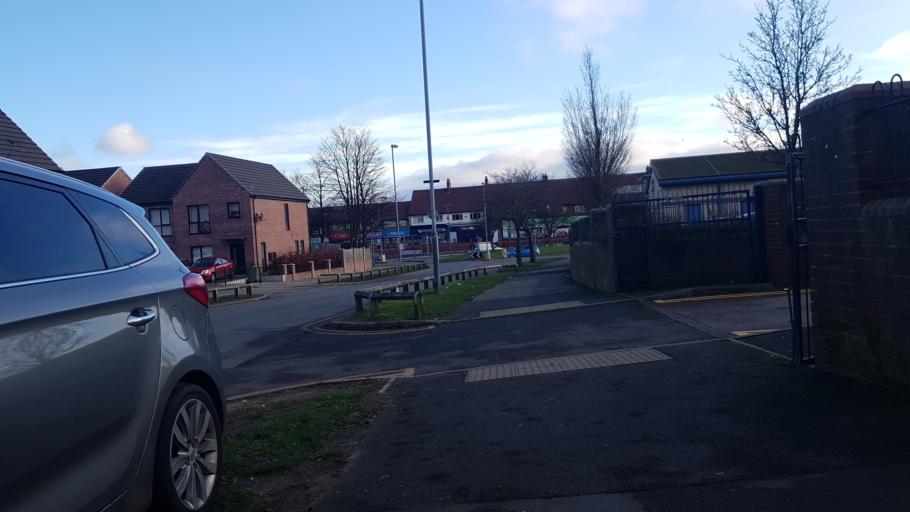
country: GB
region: England
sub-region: City and Borough of Wakefield
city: Pontefract
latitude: 53.7244
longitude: -1.3164
